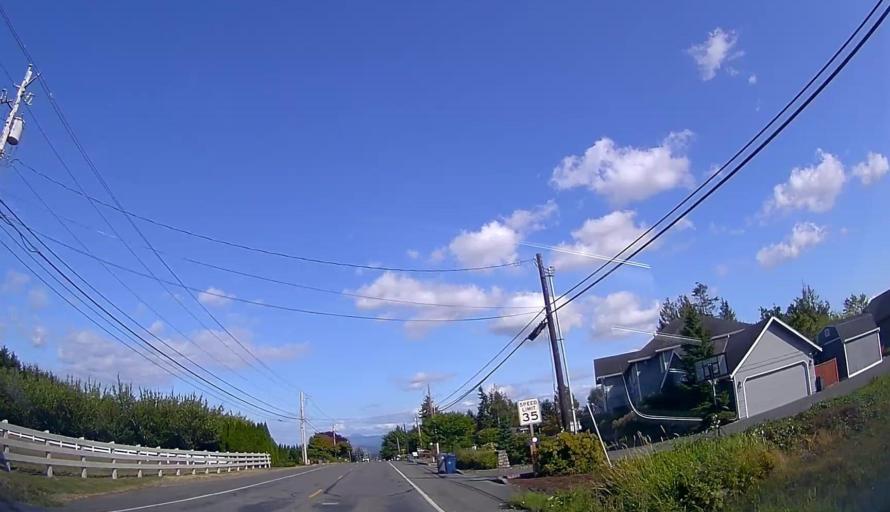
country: US
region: Washington
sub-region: Skagit County
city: Burlington
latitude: 48.4721
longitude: -122.3901
